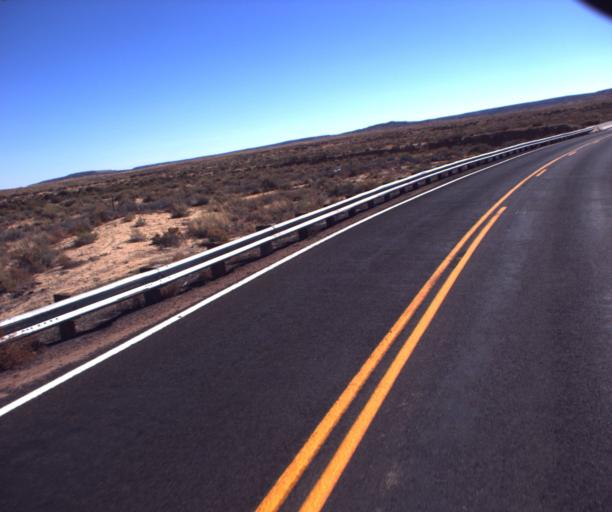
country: US
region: Arizona
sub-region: Navajo County
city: First Mesa
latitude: 35.9838
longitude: -110.7082
